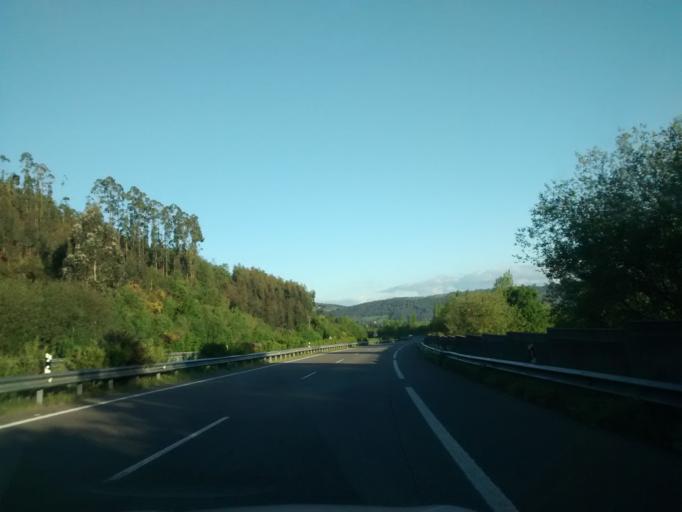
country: ES
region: Asturias
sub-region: Province of Asturias
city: Villaviciosa
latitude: 43.4978
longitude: -5.3804
